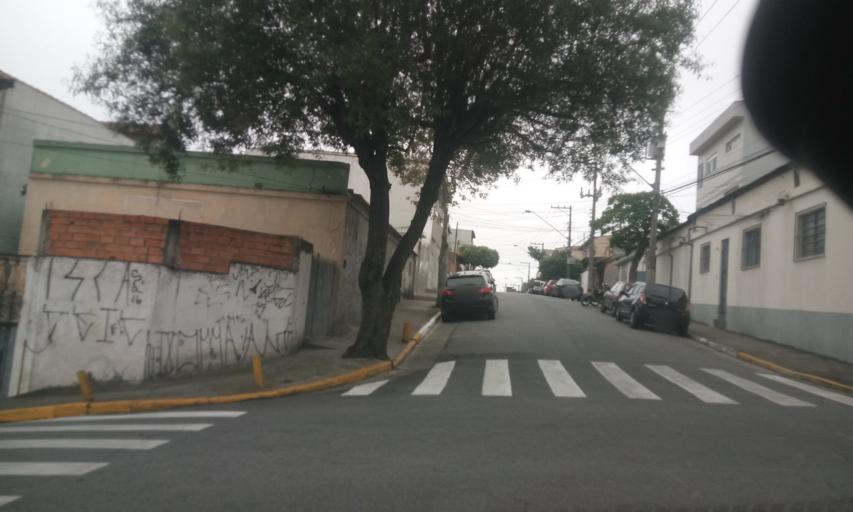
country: BR
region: Sao Paulo
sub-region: Sao Caetano Do Sul
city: Sao Caetano do Sul
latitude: -23.6413
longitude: -46.5688
